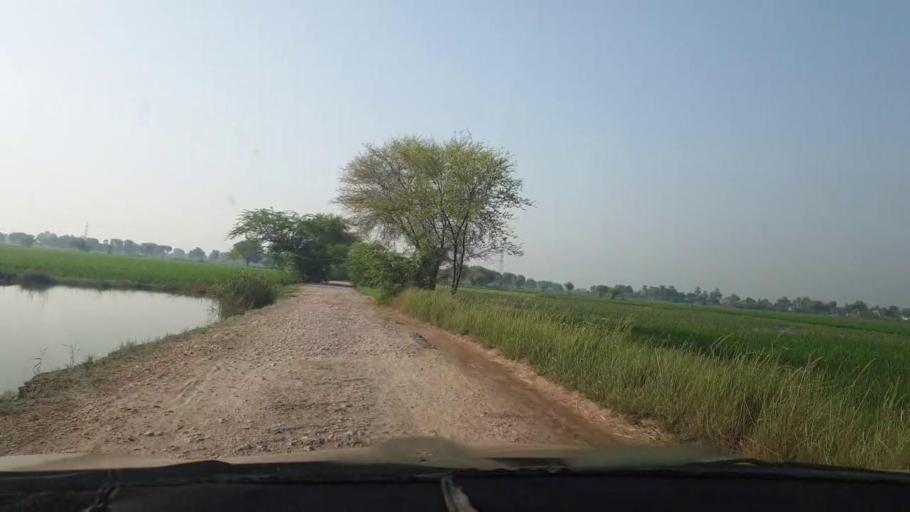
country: PK
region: Sindh
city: Kambar
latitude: 27.5773
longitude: 68.1023
